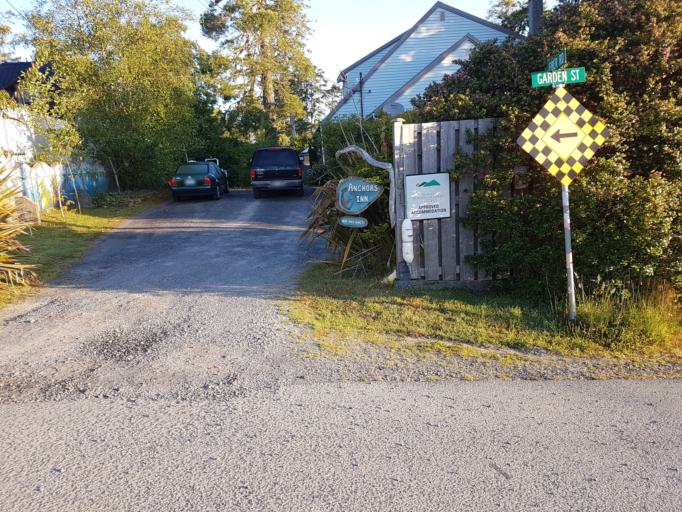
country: CA
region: British Columbia
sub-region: Regional District of Alberni-Clayoquot
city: Ucluelet
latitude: 48.9393
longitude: -125.5399
